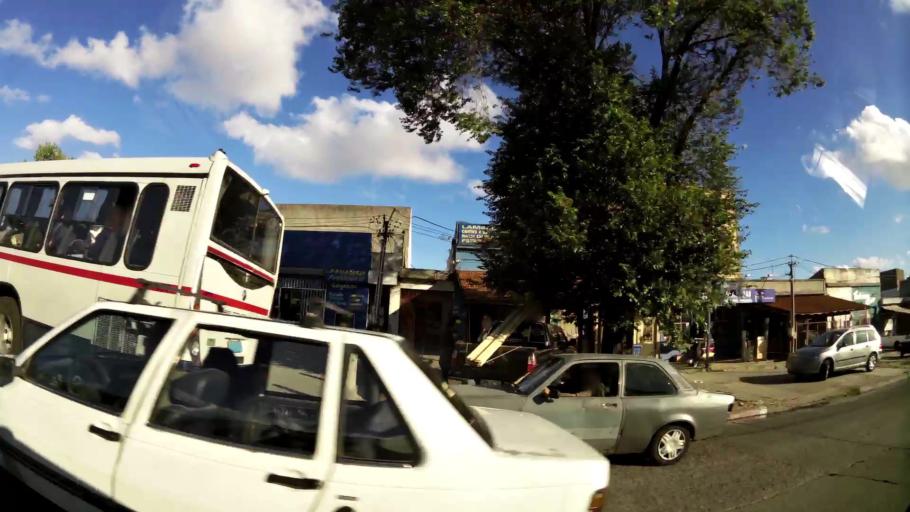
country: UY
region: Montevideo
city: Montevideo
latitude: -34.8692
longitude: -56.2399
